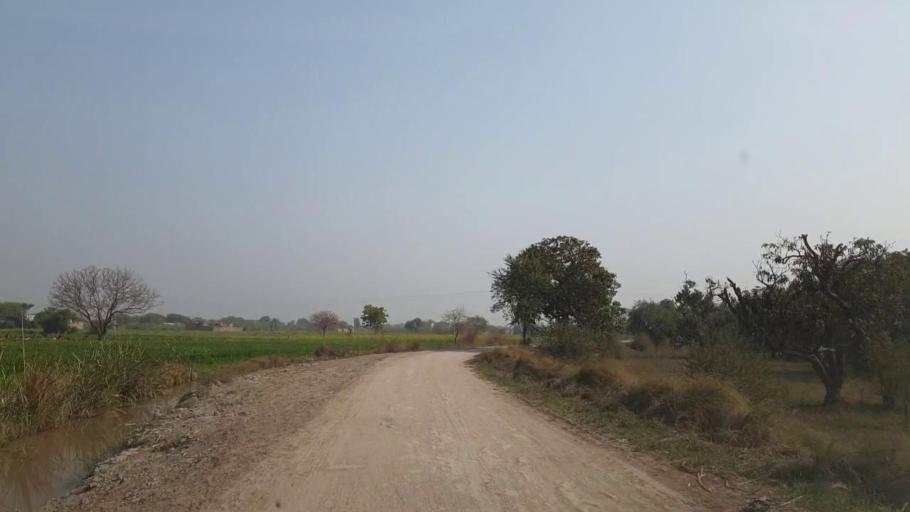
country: PK
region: Sindh
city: Mirpur Khas
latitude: 25.5544
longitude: 69.0182
